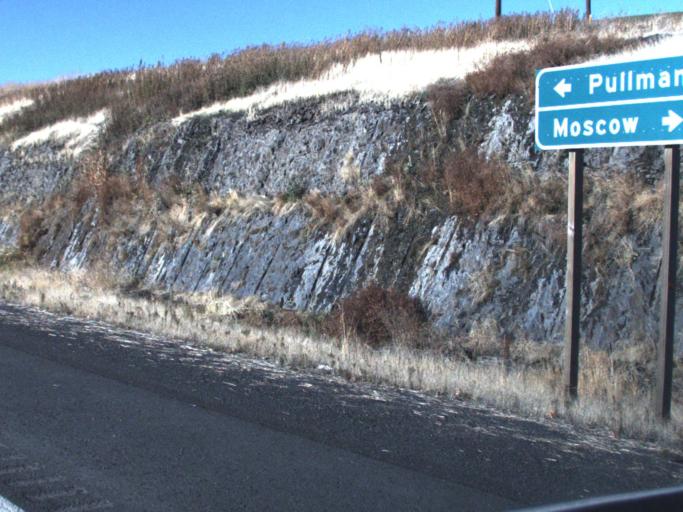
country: US
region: Idaho
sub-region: Latah County
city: Moscow
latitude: 46.7316
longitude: -117.0883
